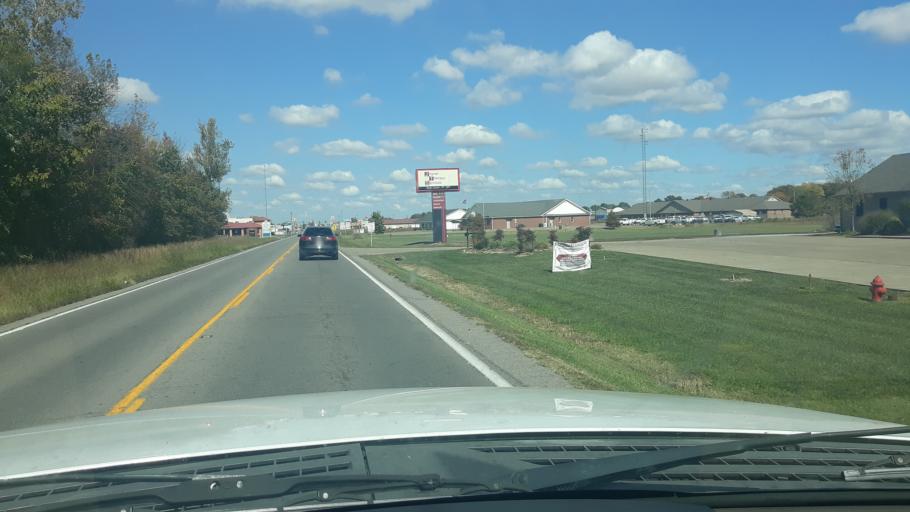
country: US
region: Illinois
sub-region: Saline County
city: Harrisburg
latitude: 37.7227
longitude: -88.5390
